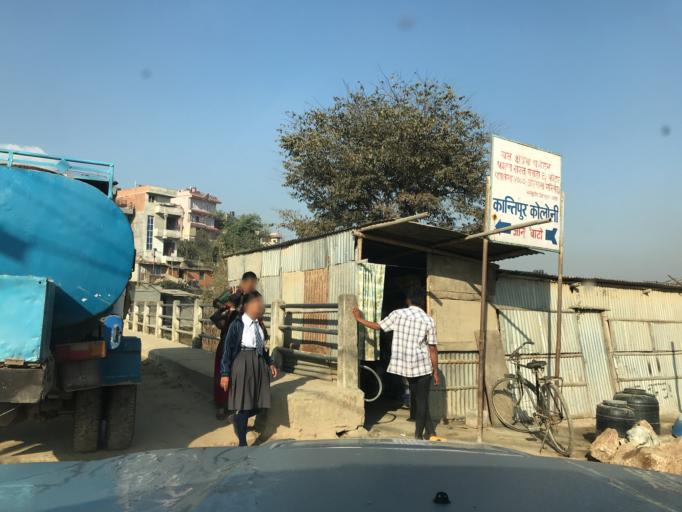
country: NP
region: Central Region
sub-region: Bagmati Zone
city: Patan
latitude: 27.6508
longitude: 85.3127
